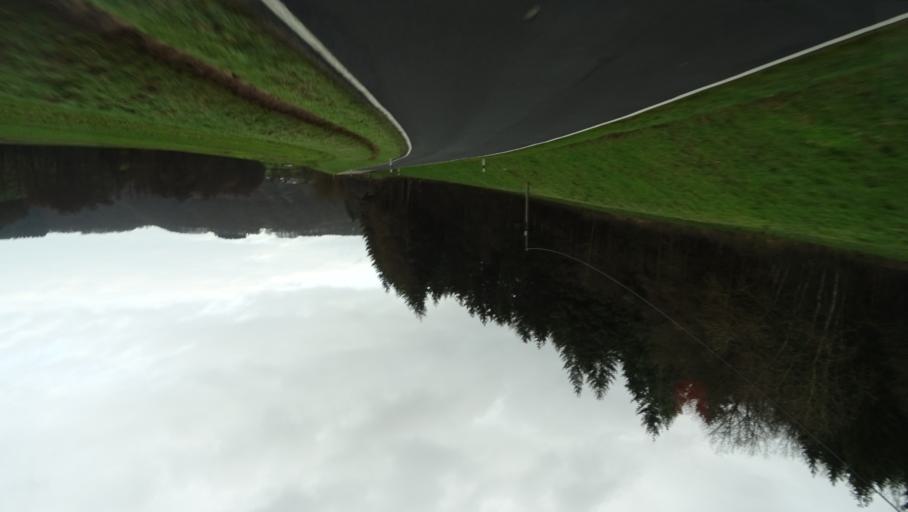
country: DE
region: Baden-Wuerttemberg
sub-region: Karlsruhe Region
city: Neckargerach
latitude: 49.3876
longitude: 9.0593
